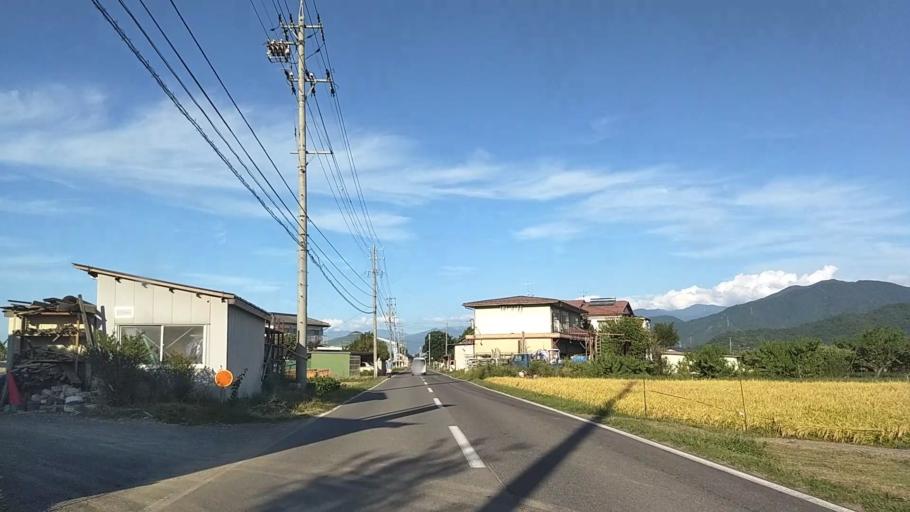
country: JP
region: Nagano
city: Nagano-shi
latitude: 36.6005
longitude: 138.1989
